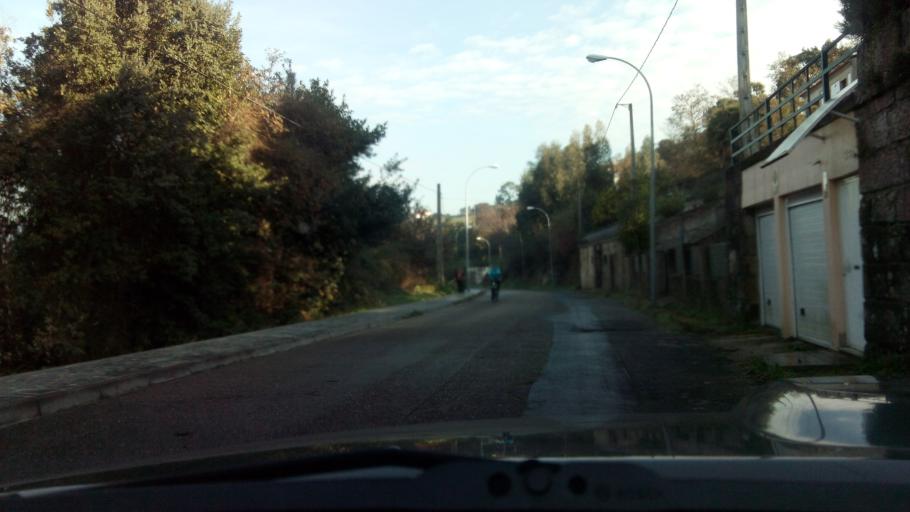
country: ES
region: Galicia
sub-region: Provincia de Pontevedra
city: Marin
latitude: 42.3745
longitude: -8.7303
